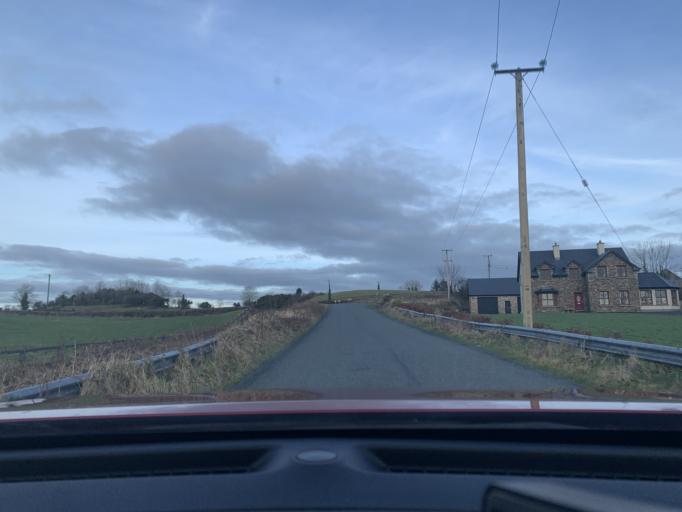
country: IE
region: Connaught
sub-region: Sligo
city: Ballymote
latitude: 54.1261
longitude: -8.5862
